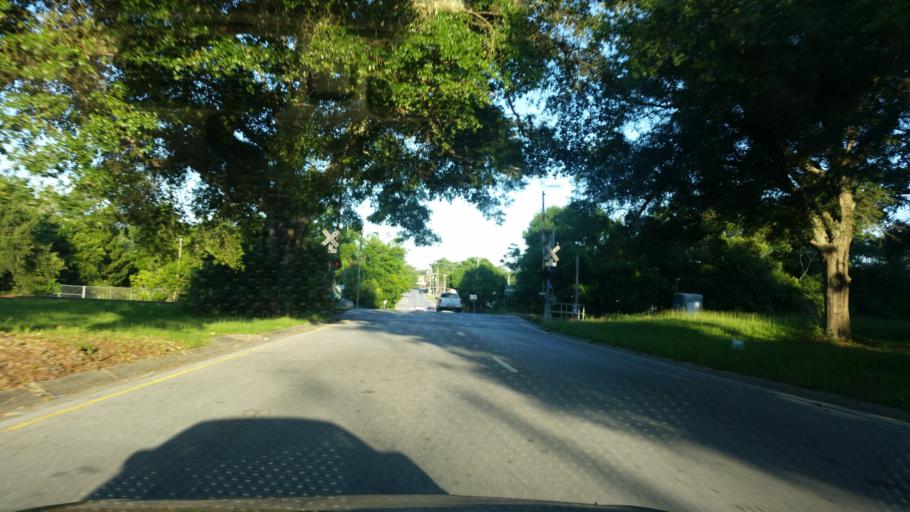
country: US
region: Florida
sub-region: Escambia County
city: Goulding
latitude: 30.4349
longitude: -87.2182
